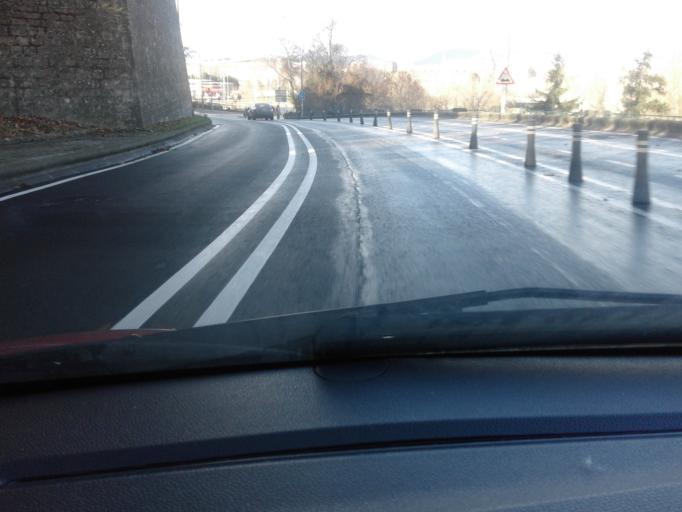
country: ES
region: Navarre
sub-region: Provincia de Navarra
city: Primer Ensanche
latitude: 42.8190
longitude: -1.6512
